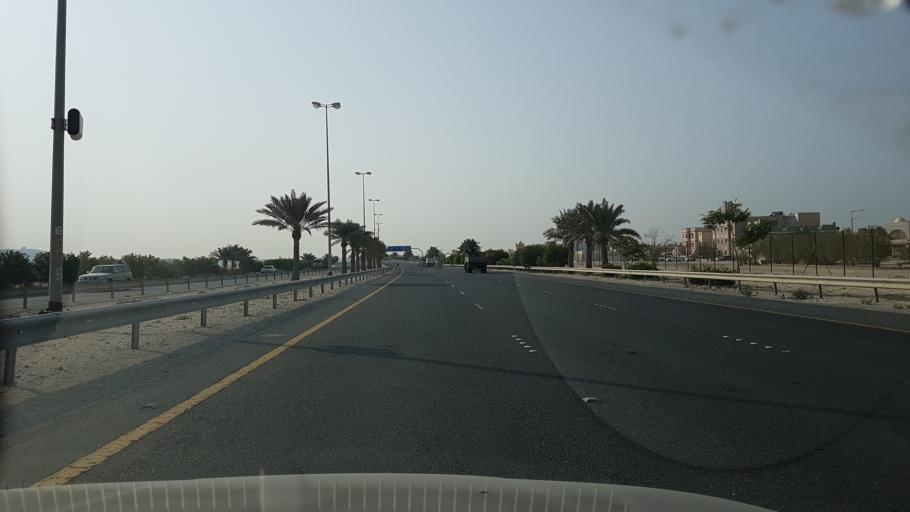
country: BH
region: Central Governorate
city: Dar Kulayb
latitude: 26.0721
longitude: 50.5148
